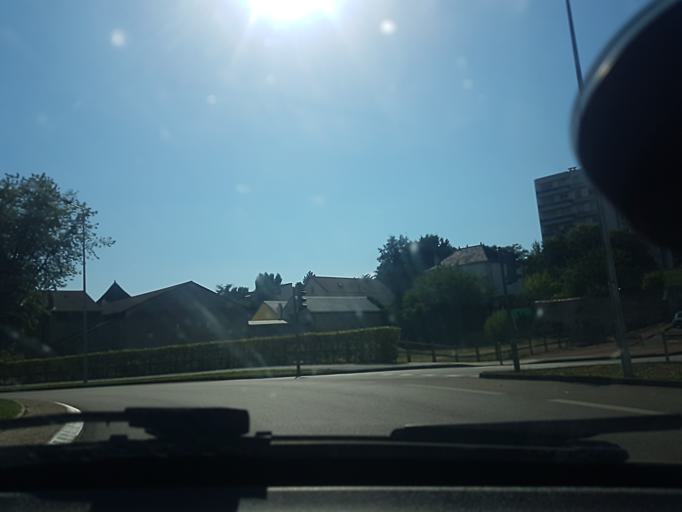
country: FR
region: Bourgogne
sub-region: Departement de Saone-et-Loire
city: Chalon-sur-Saone
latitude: 46.7908
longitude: 4.8622
